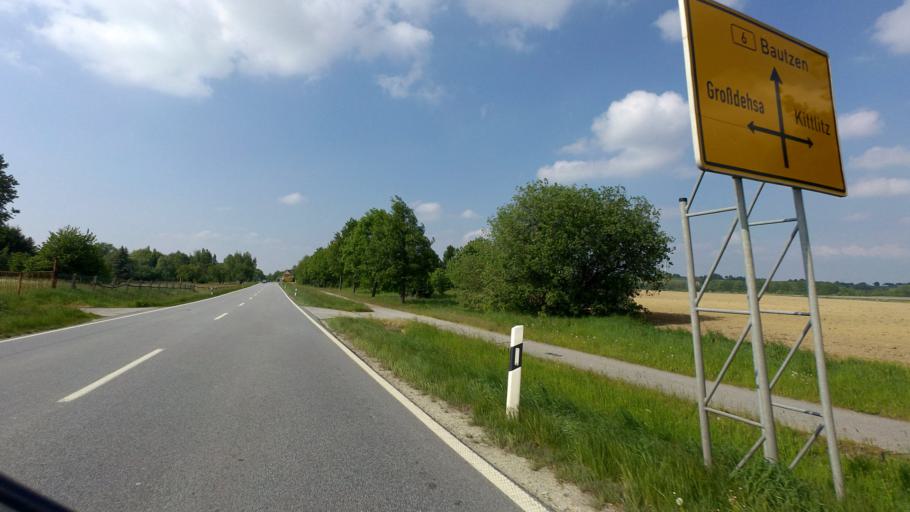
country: DE
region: Saxony
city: Lobau
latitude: 51.1149
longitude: 14.6455
